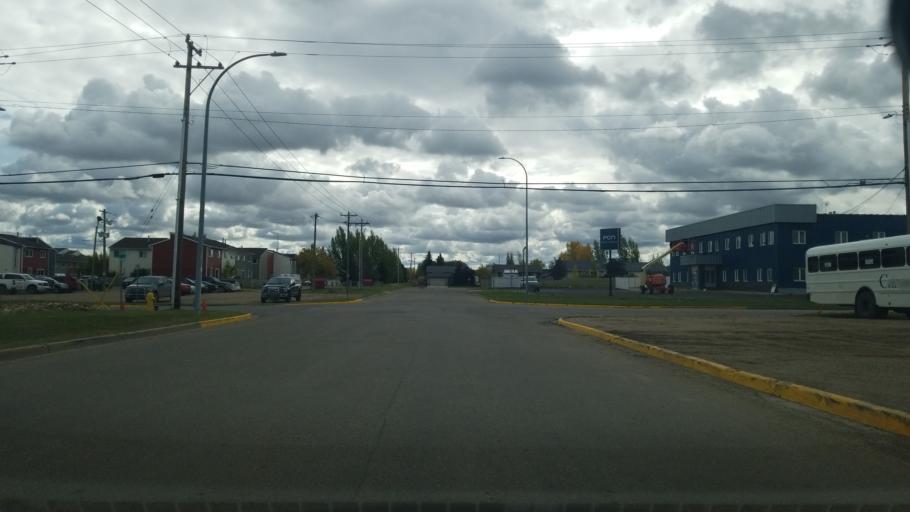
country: CA
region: Saskatchewan
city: Lloydminster
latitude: 53.2772
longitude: -110.0299
